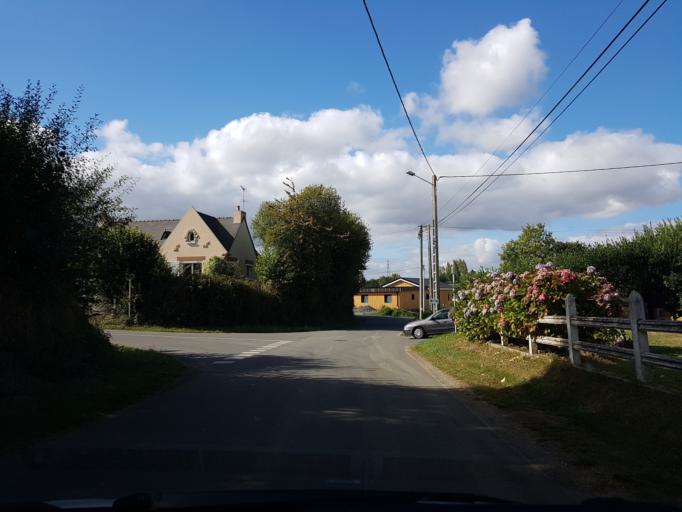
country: FR
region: Brittany
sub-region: Departement des Cotes-d'Armor
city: Pledran
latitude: 48.4683
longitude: -2.7625
